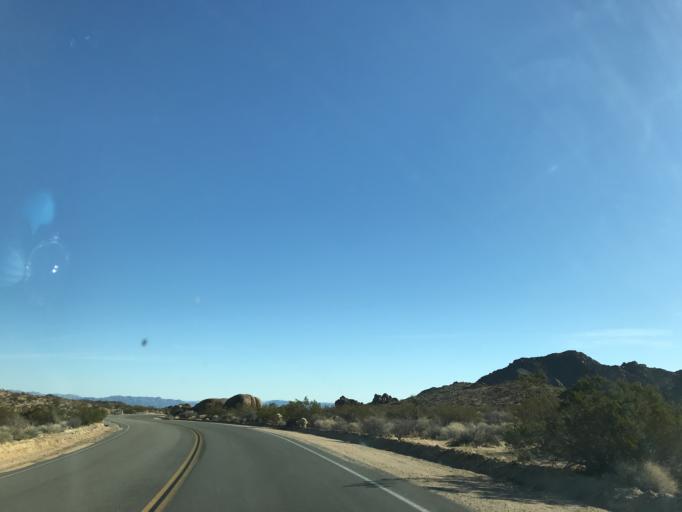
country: US
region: California
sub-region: Riverside County
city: Mecca
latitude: 33.7806
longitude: -115.7985
